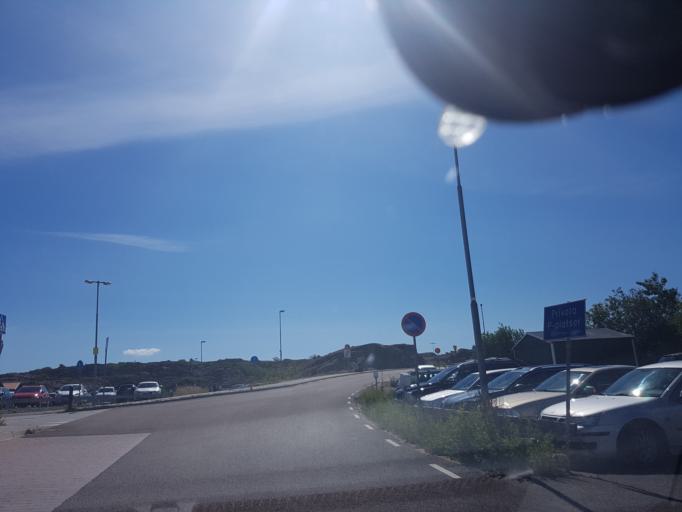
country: SE
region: Vaestra Goetaland
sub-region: Lysekils Kommun
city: Lysekil
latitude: 58.1747
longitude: 11.4162
